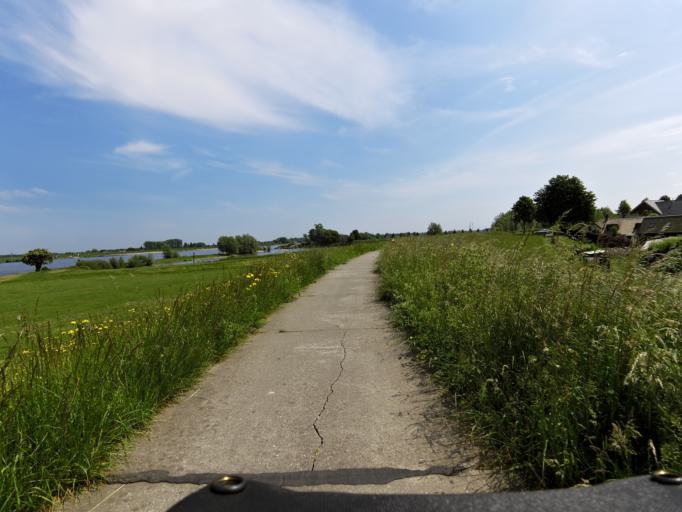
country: NL
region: South Holland
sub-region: Gemeente Leerdam
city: Leerdam
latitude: 51.8239
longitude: 5.0852
